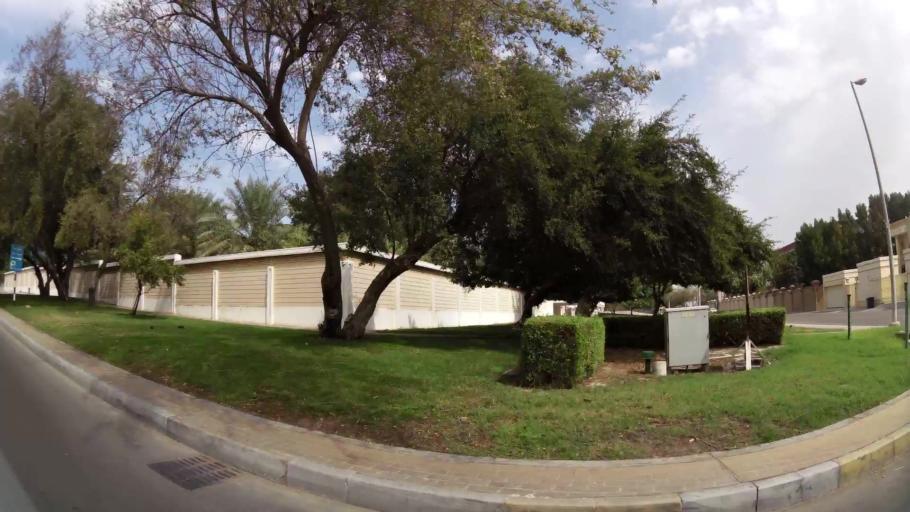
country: AE
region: Abu Dhabi
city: Abu Dhabi
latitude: 24.4644
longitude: 54.3423
